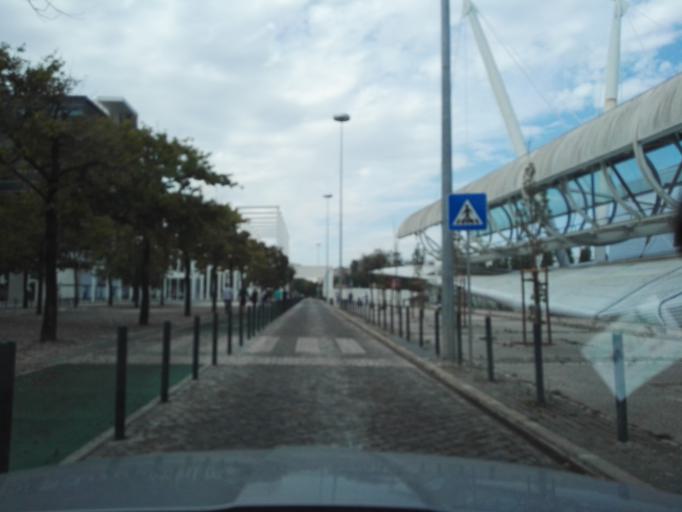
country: PT
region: Lisbon
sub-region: Loures
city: Moscavide
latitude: 38.7730
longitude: -9.0950
